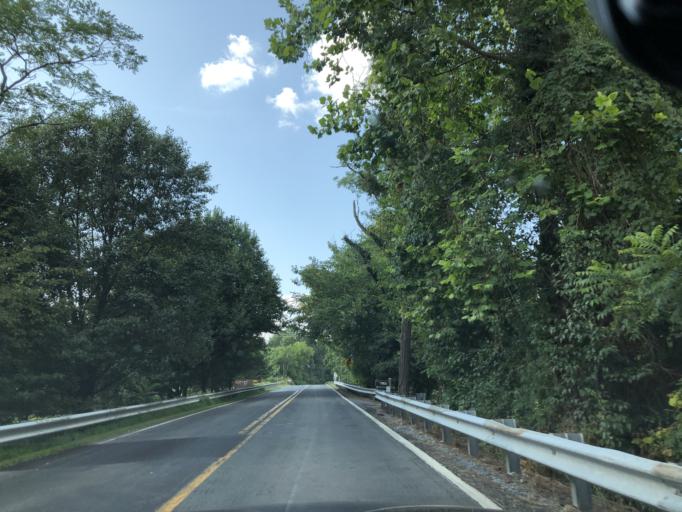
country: US
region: Maryland
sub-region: Carroll County
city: Mount Airy
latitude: 39.4034
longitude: -77.1788
